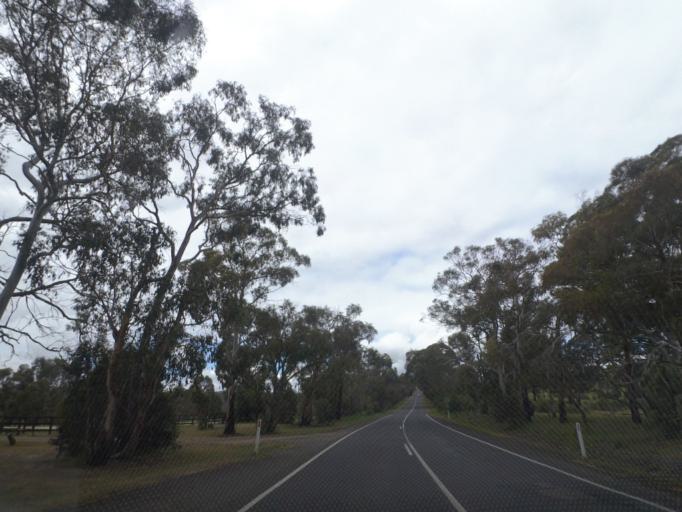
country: AU
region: Victoria
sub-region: Hume
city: Craigieburn
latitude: -37.3944
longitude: 144.9342
